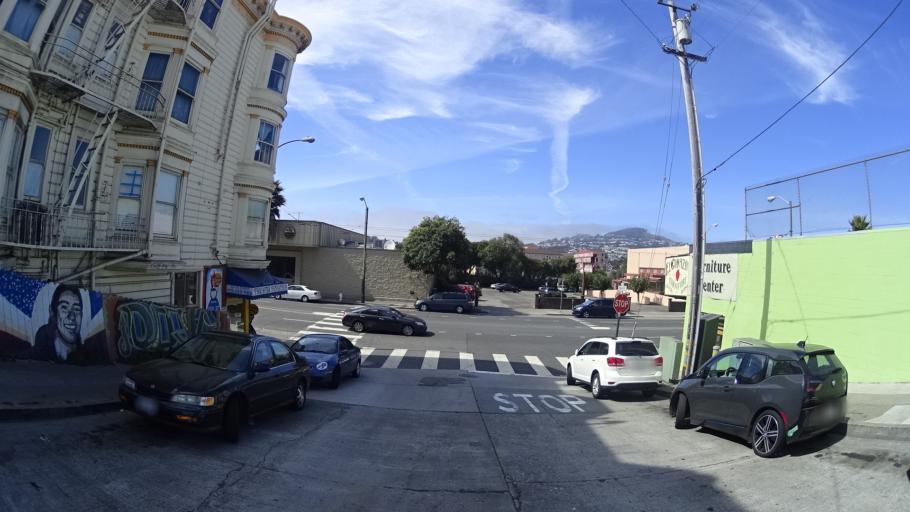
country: US
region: California
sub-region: San Mateo County
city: Daly City
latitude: 37.7199
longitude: -122.4381
